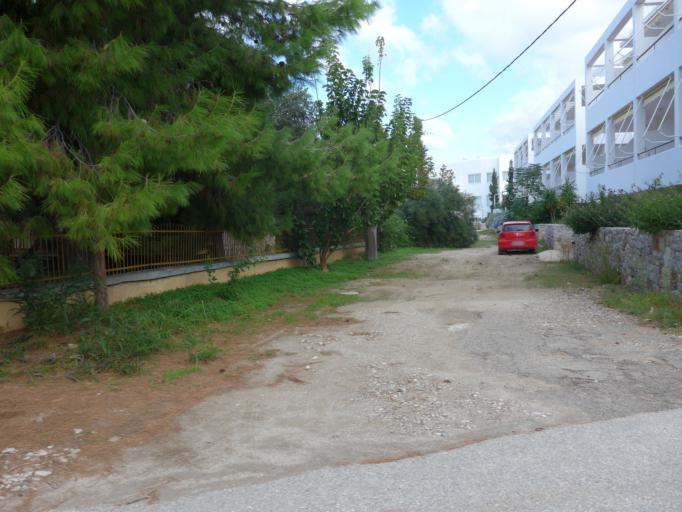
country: GR
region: Peloponnese
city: Asklipieio
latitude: 37.4931
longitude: 22.9909
